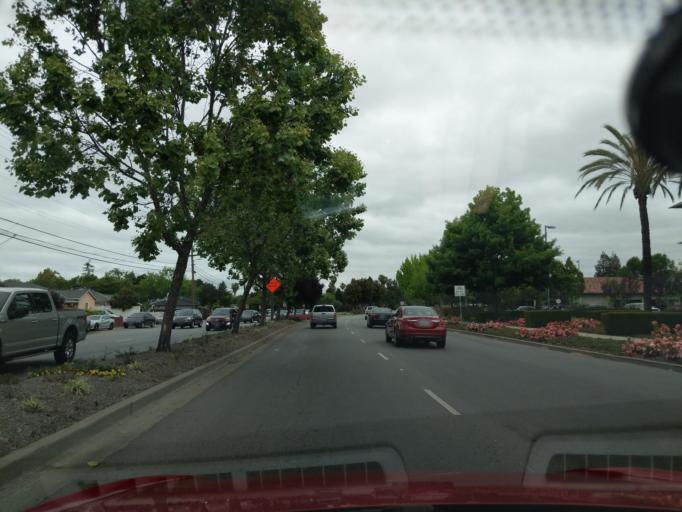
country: US
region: California
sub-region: San Mateo County
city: North Fair Oaks
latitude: 37.4795
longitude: -122.1852
